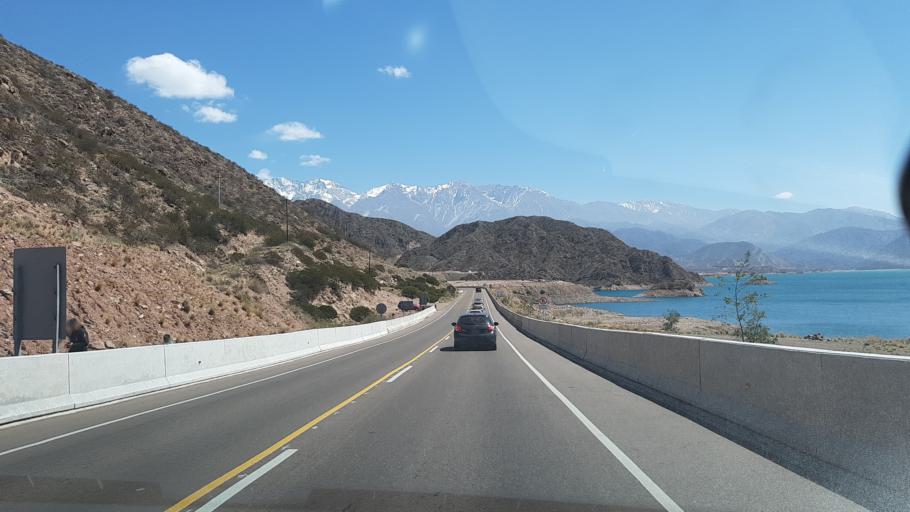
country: AR
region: Mendoza
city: Lujan de Cuyo
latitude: -32.9968
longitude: -69.1386
